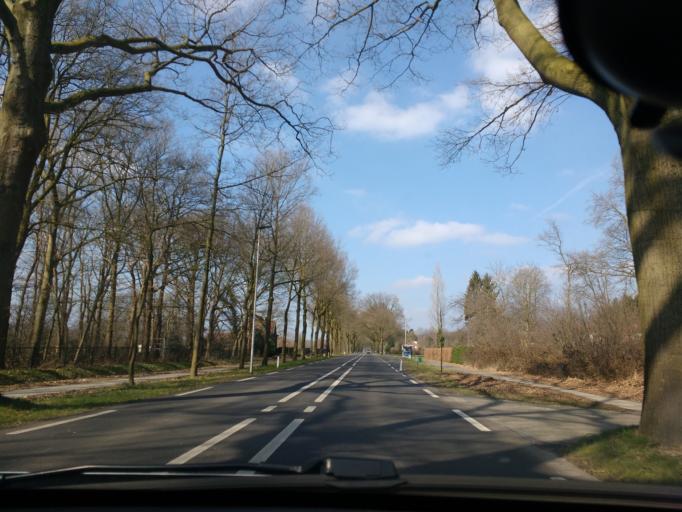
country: NL
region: Gelderland
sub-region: Gemeente Groesbeek
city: Bredeweg
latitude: 51.7262
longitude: 5.9441
